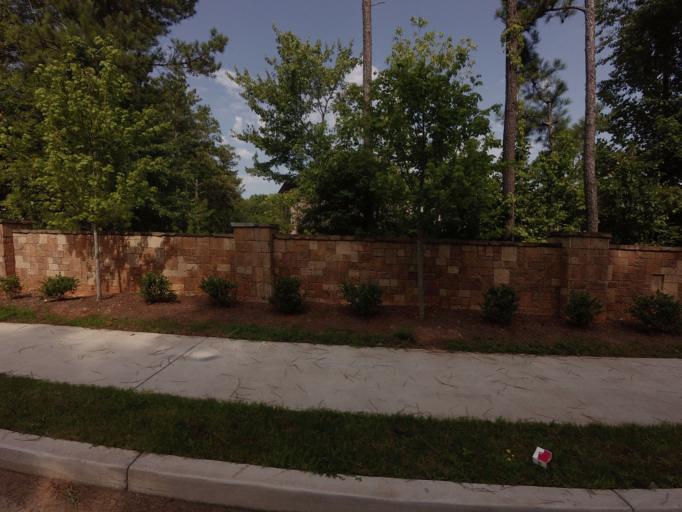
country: US
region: Georgia
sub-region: Fulton County
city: Johns Creek
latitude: 34.0391
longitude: -84.2345
